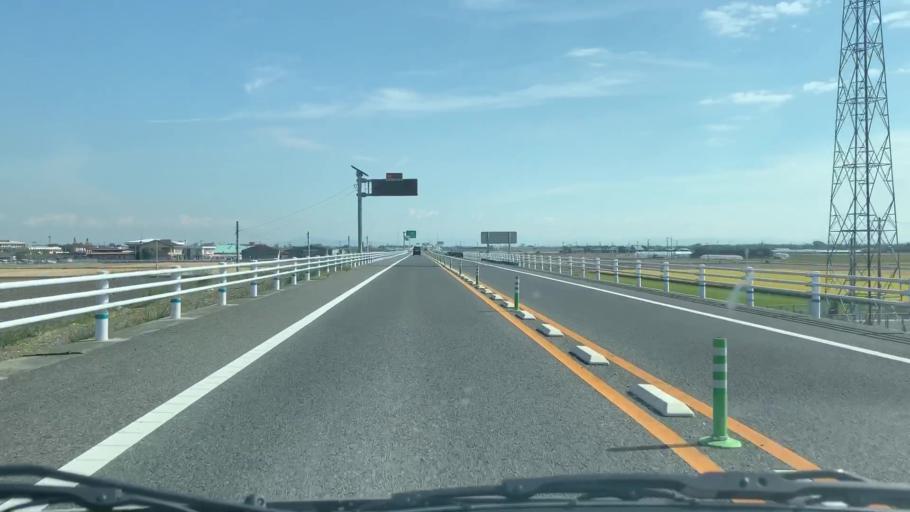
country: JP
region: Saga Prefecture
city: Saga-shi
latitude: 33.2309
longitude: 130.2323
